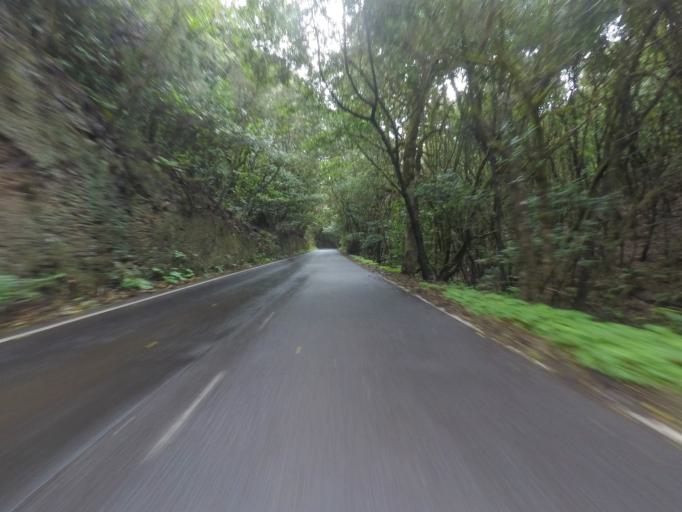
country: ES
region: Canary Islands
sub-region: Provincia de Santa Cruz de Tenerife
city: Vallehermosa
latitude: 28.1600
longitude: -17.2980
